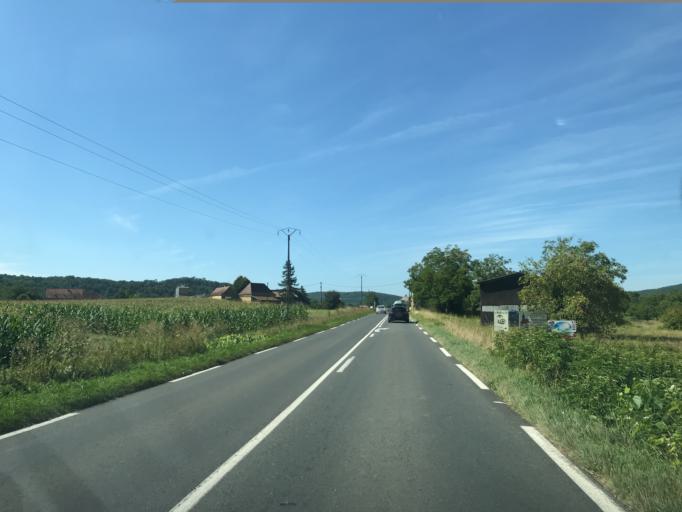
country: FR
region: Aquitaine
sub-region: Departement de la Dordogne
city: Cenac-et-Saint-Julien
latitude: 44.8381
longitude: 1.1691
